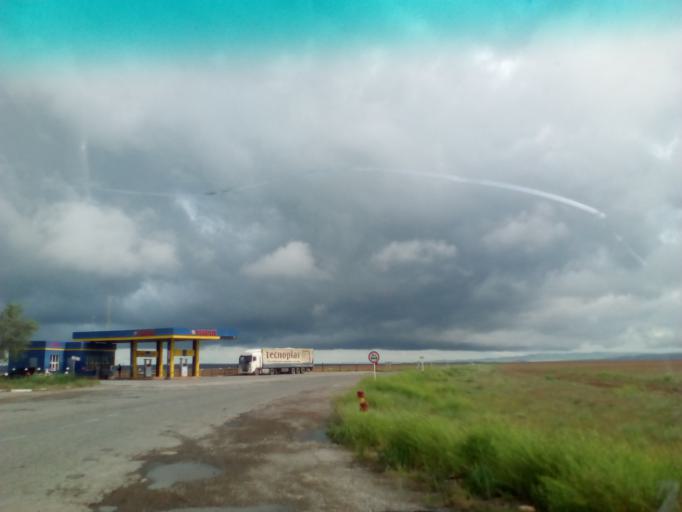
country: KZ
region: Ongtustik Qazaqstan
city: Sholaqqkorghan
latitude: 43.7001
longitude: 69.2379
